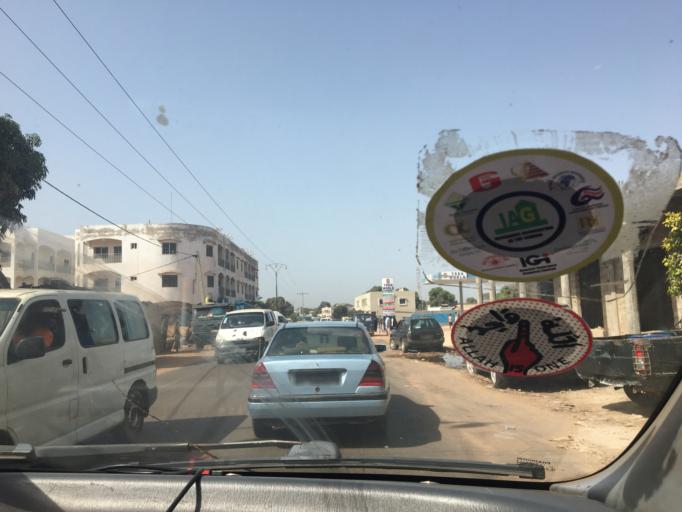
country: GM
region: Western
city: Abuko
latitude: 13.3846
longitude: -16.6782
